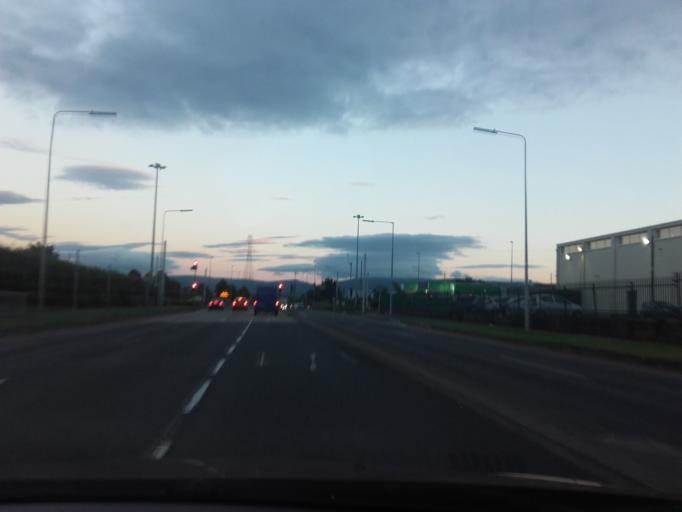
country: IE
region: Leinster
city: Tallaght
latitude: 53.3013
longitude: -6.3747
